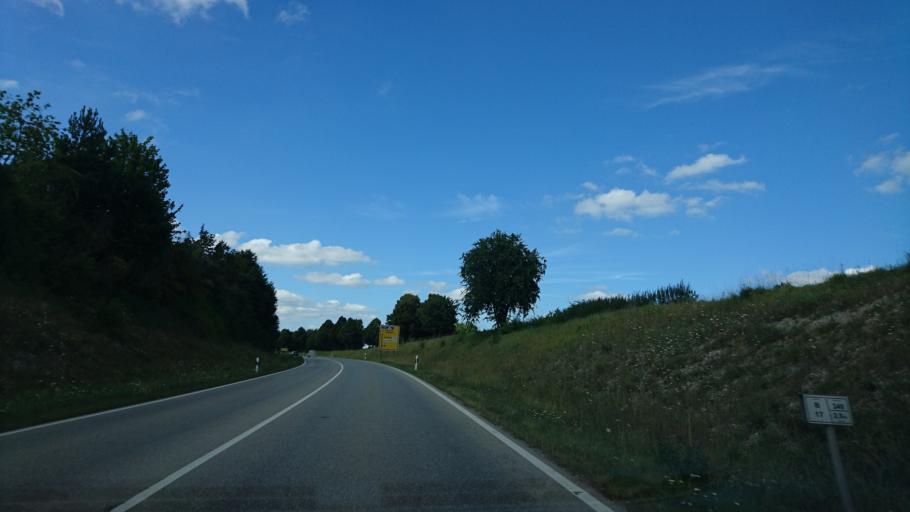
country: DE
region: Bavaria
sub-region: Upper Bavaria
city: Hohenfurch
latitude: 47.8380
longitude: 10.9013
